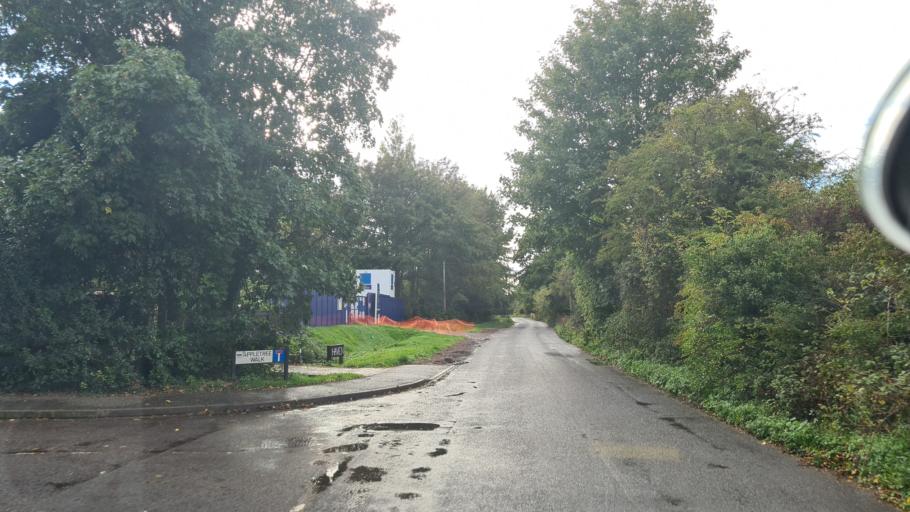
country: GB
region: England
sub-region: West Sussex
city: Littlehampton
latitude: 50.8119
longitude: -0.5849
